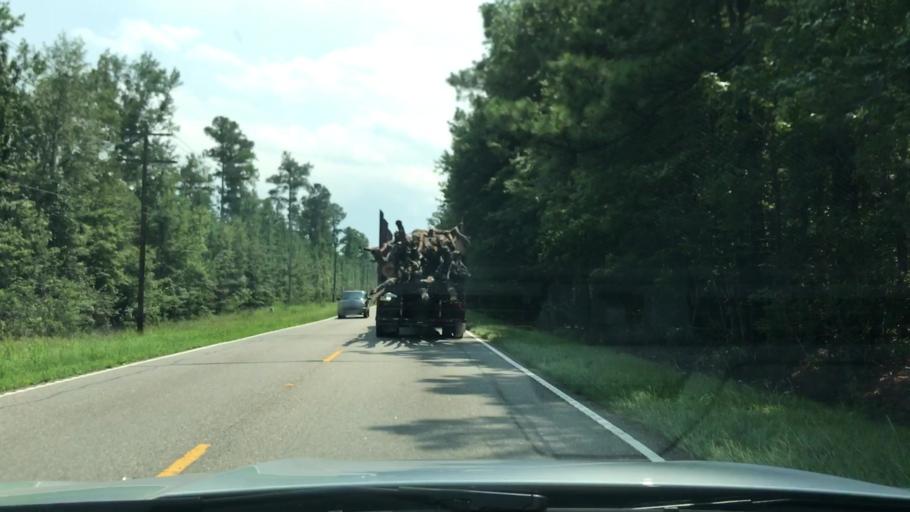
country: US
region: South Carolina
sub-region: Georgetown County
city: Georgetown
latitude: 33.4450
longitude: -79.2779
